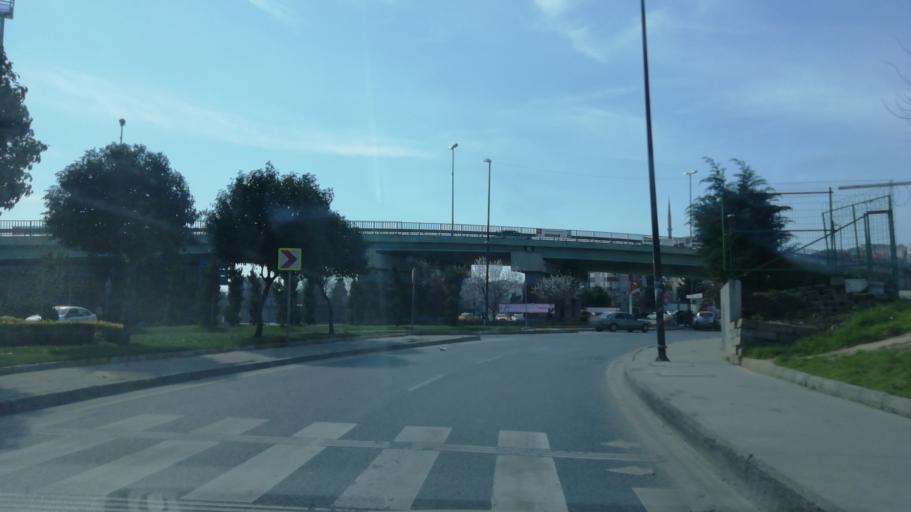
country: TR
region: Istanbul
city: Bahcelievler
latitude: 41.0140
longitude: 28.8482
